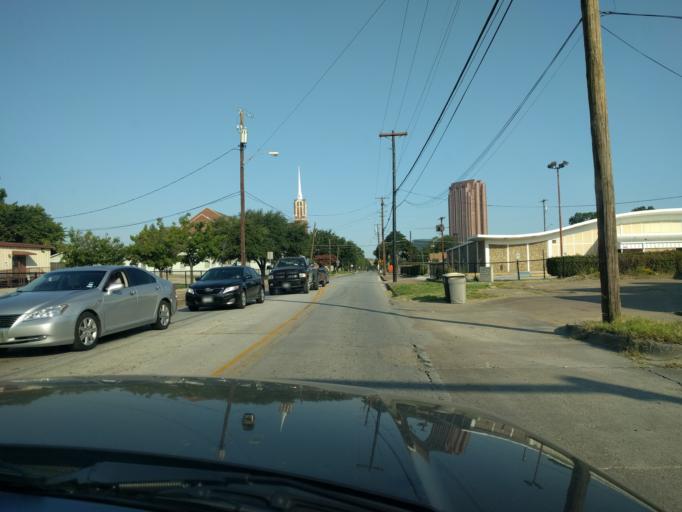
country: US
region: Texas
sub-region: Dallas County
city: Dallas
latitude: 32.7980
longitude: -96.7863
